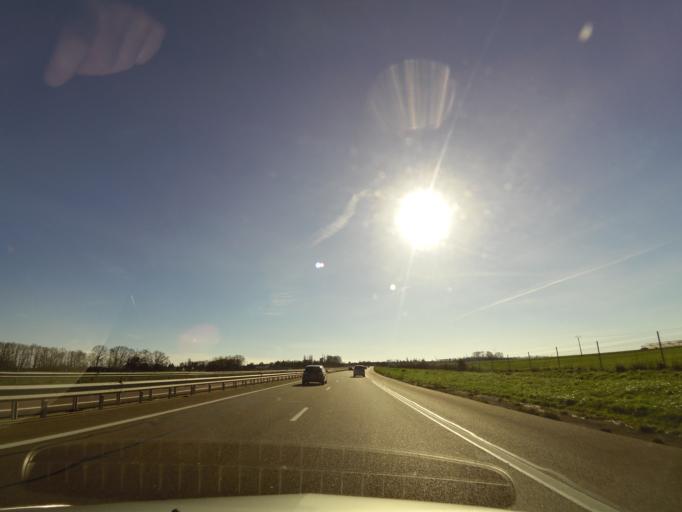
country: FR
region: Bourgogne
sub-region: Departement de l'Yonne
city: Venoy
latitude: 47.8253
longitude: 3.6239
